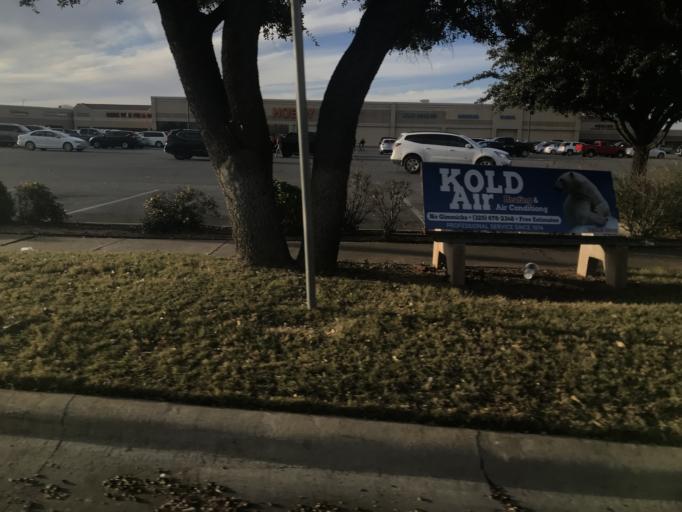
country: US
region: Texas
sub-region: Taylor County
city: Abilene
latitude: 32.4303
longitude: -99.7828
